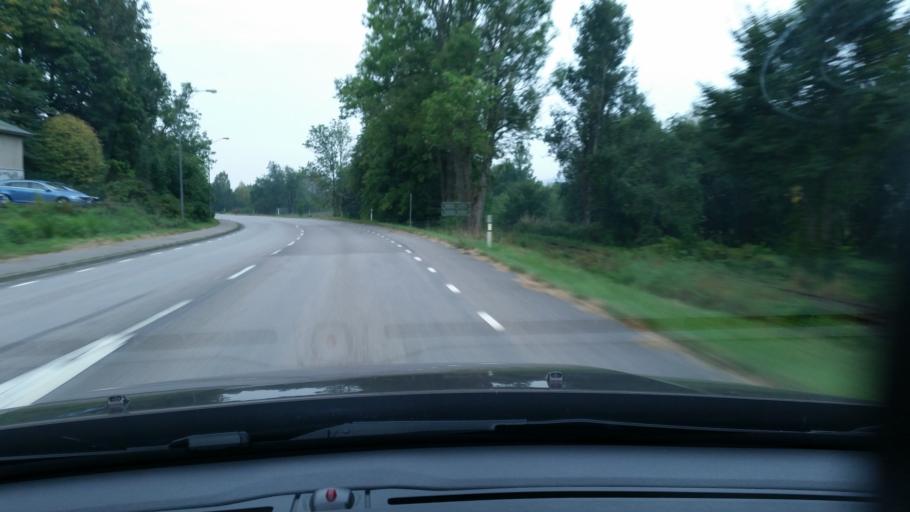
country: SE
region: Vaestra Goetaland
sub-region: Lilla Edets Kommun
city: Lodose
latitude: 58.0331
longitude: 12.1513
